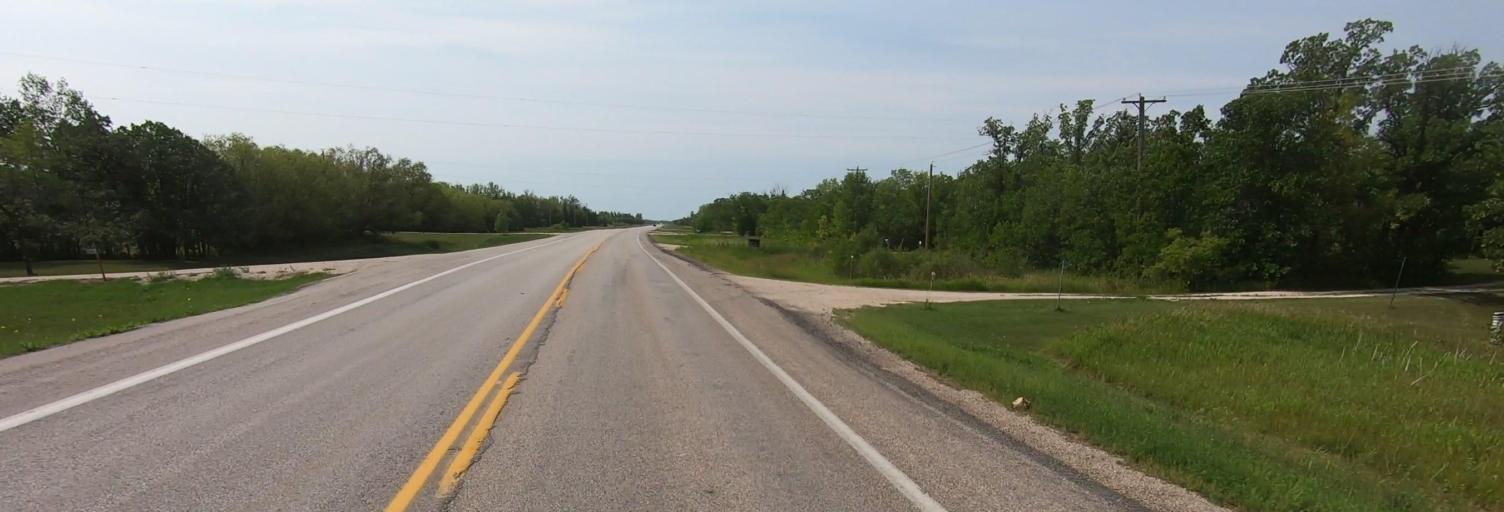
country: CA
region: Manitoba
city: Niverville
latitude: 49.6321
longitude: -97.1095
